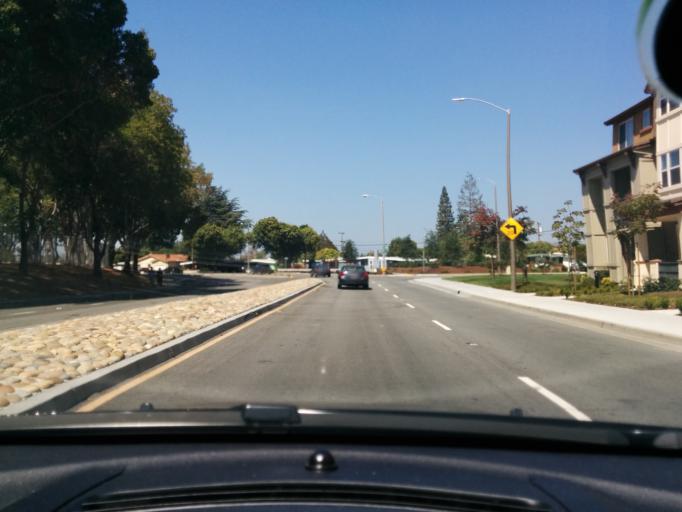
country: US
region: California
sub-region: Santa Clara County
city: Sunnyvale
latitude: 37.3877
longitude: -121.9985
